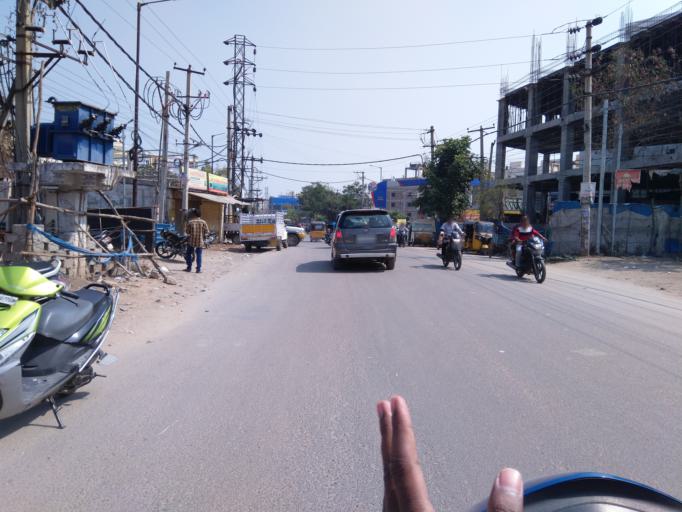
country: IN
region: Telangana
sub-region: Rangareddi
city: Kukatpalli
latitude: 17.4987
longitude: 78.4122
